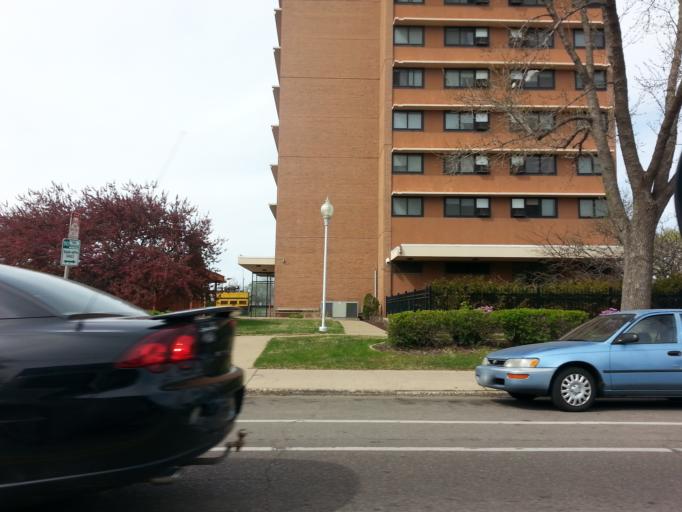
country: US
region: Minnesota
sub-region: Hennepin County
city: Minneapolis
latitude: 44.9628
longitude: -93.2320
